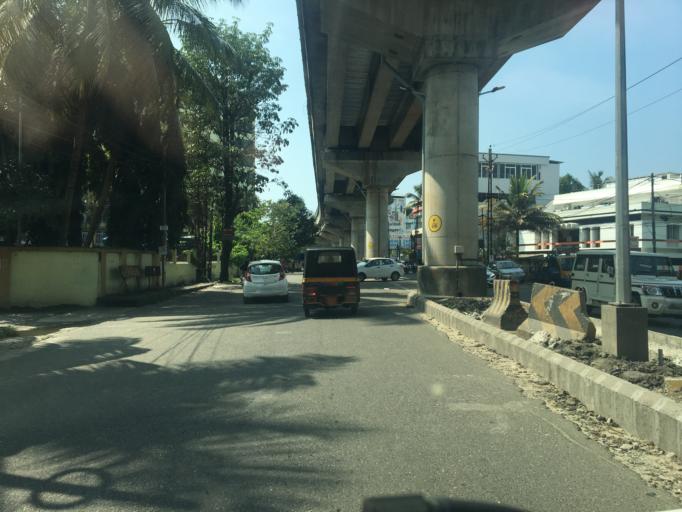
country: IN
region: Kerala
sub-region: Ernakulam
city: Cochin
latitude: 9.9671
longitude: 76.3067
